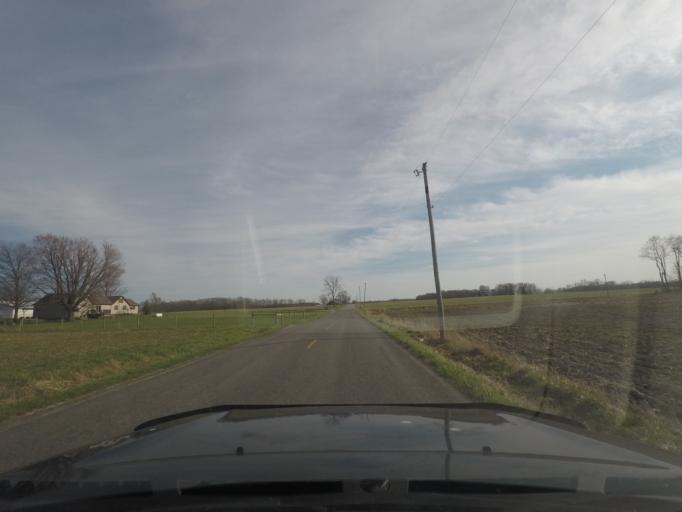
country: US
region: Indiana
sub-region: Elkhart County
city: Dunlap
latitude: 41.5668
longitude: -85.9250
